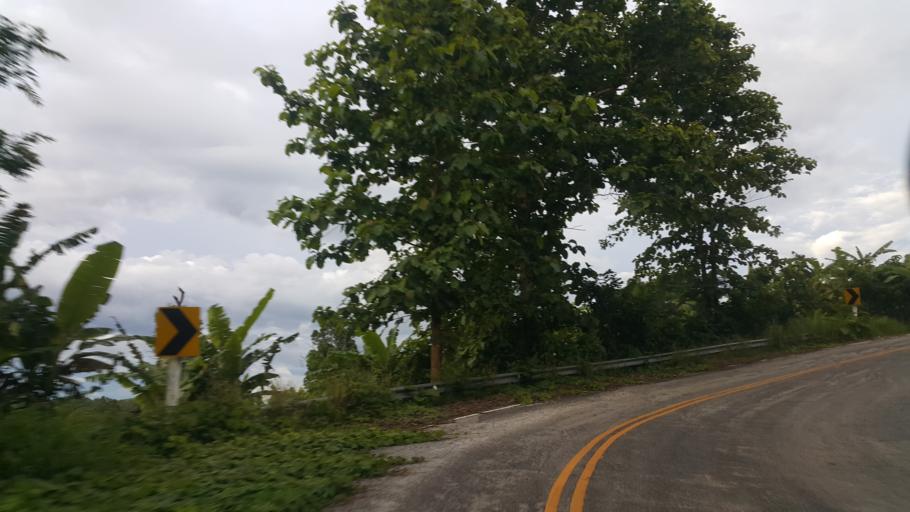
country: TH
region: Loei
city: Na Haeo
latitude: 17.4772
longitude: 101.1130
